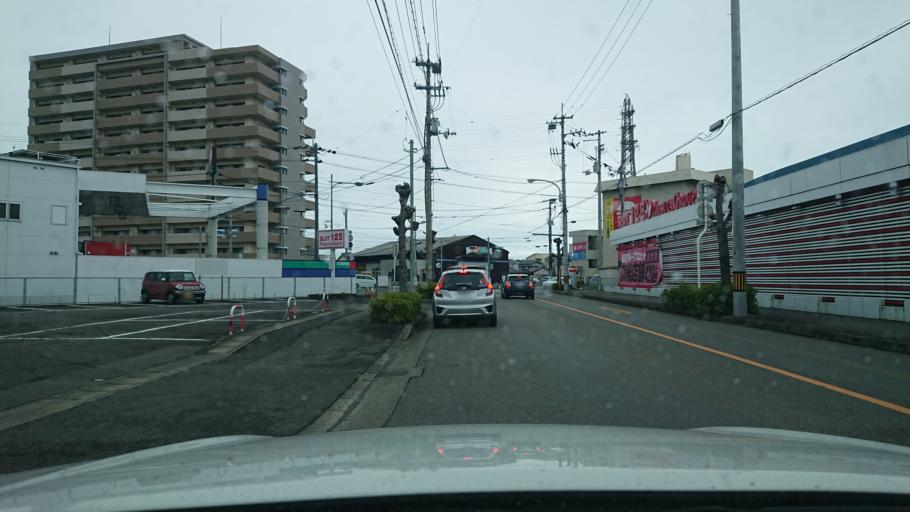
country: JP
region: Tokushima
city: Tokushima-shi
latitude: 34.0861
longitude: 134.5391
